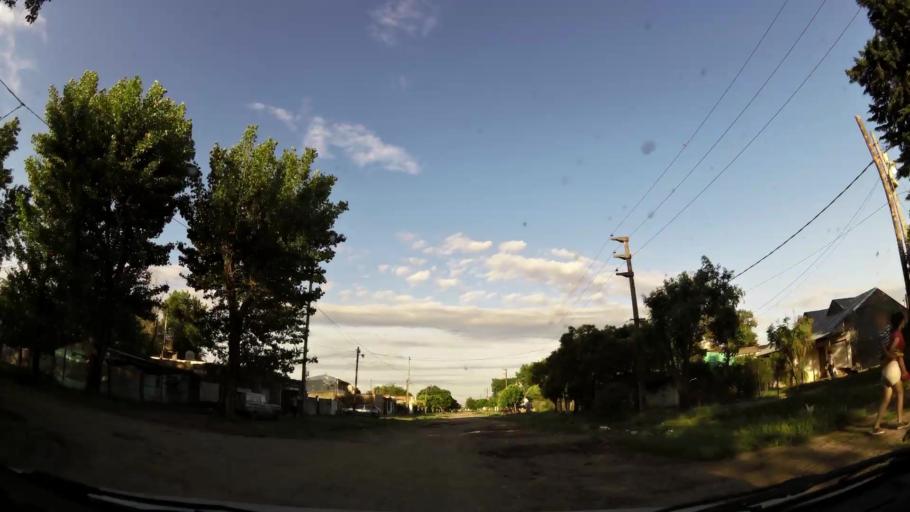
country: AR
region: Buenos Aires
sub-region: Partido de Merlo
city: Merlo
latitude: -34.6936
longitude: -58.7495
